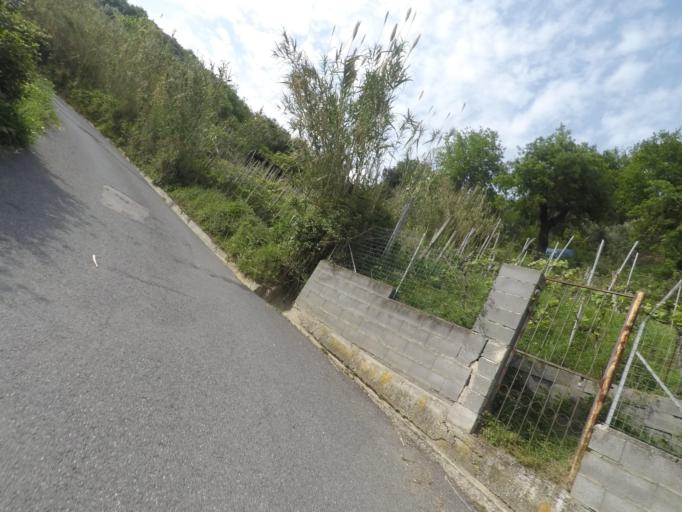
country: IT
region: Tuscany
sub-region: Provincia di Massa-Carrara
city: Massa
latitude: 44.0486
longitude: 10.0996
